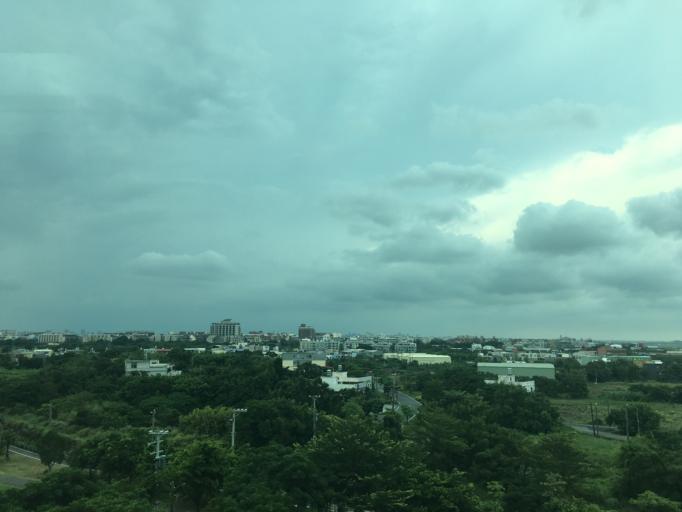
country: TW
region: Taiwan
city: Taoyuan City
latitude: 25.0875
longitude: 121.2644
